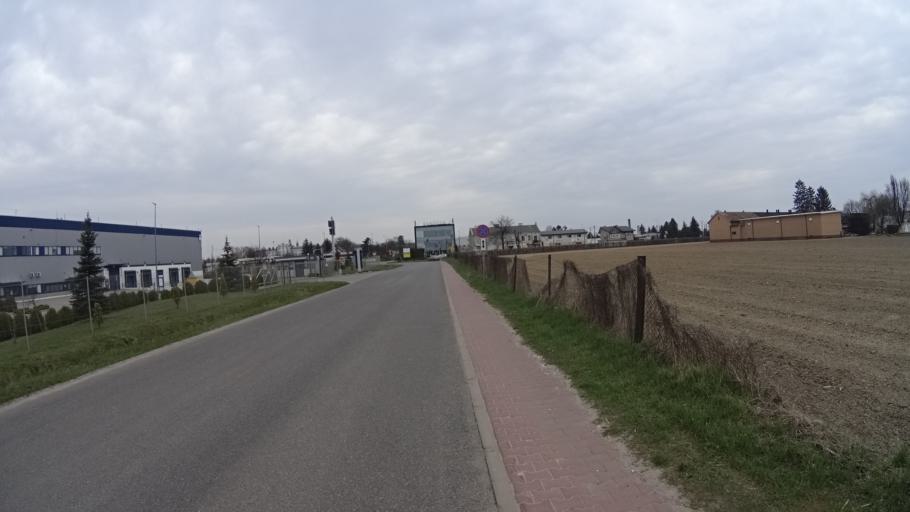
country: PL
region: Masovian Voivodeship
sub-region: Powiat warszawski zachodni
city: Ozarow Mazowiecki
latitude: 52.2096
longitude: 20.7769
